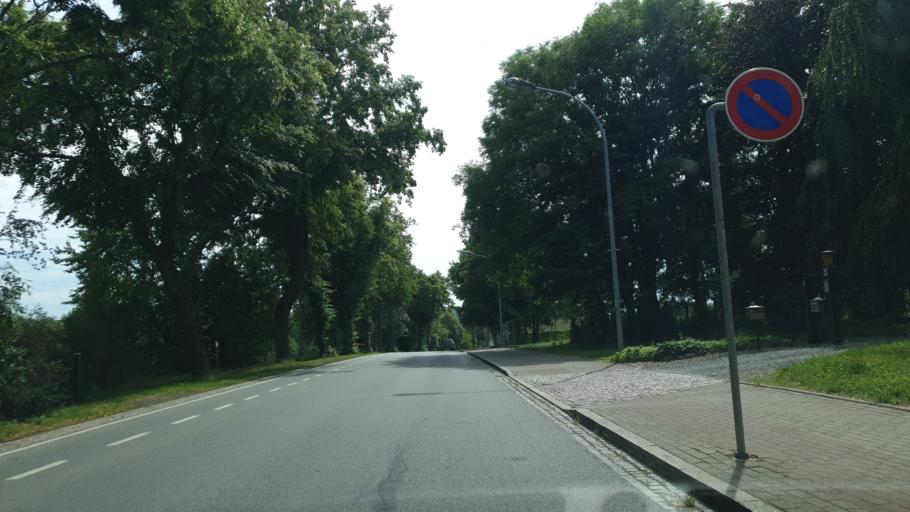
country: DE
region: Saxony
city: Oberlungwitz
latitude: 50.7932
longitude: 12.6996
